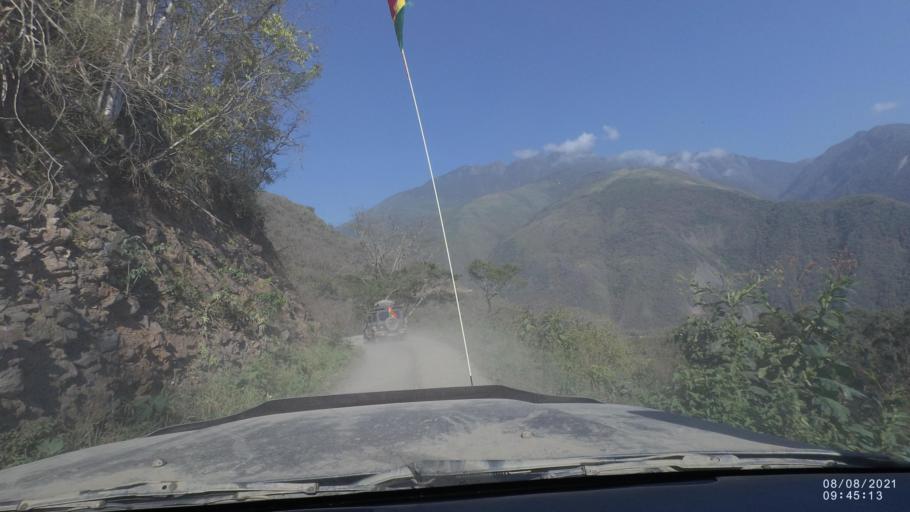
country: BO
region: La Paz
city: Quime
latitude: -16.6032
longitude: -66.7258
